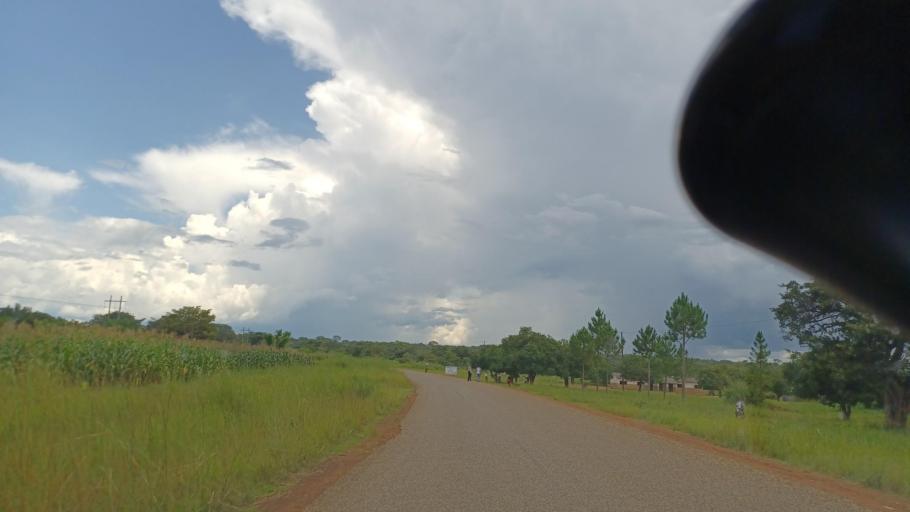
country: ZM
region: North-Western
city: Kasempa
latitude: -12.8640
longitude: 26.0377
